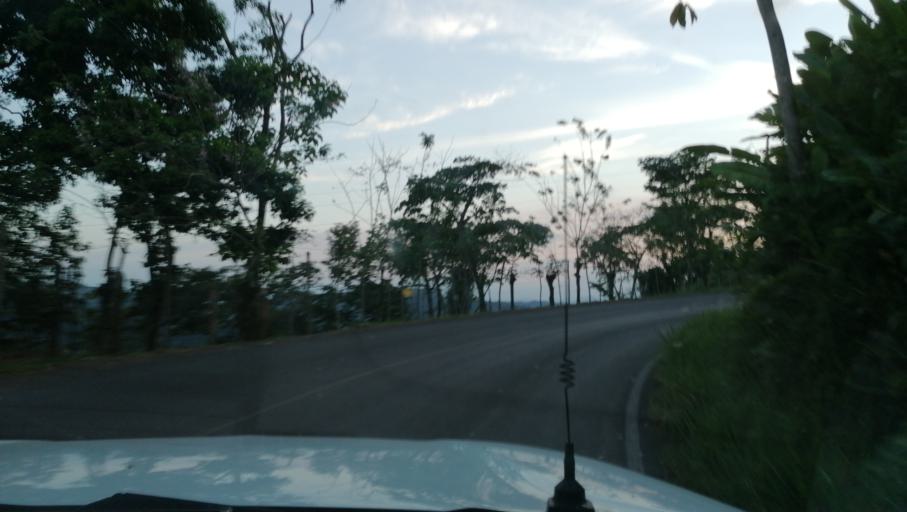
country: MX
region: Chiapas
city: Ostuacan
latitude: 17.4236
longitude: -93.3452
